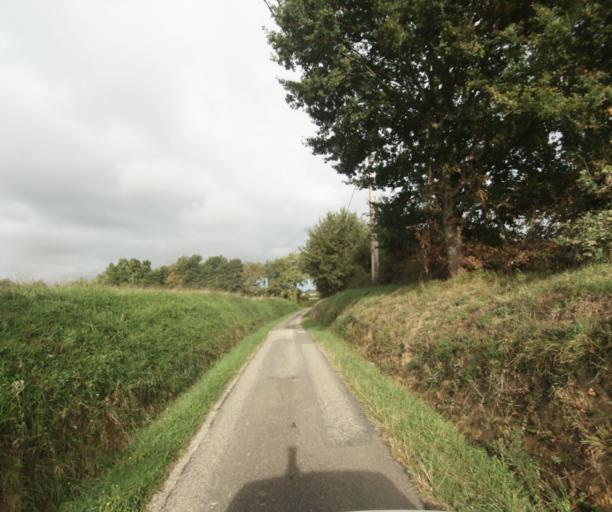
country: FR
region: Midi-Pyrenees
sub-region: Departement du Gers
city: Nogaro
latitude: 43.8201
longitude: -0.0730
